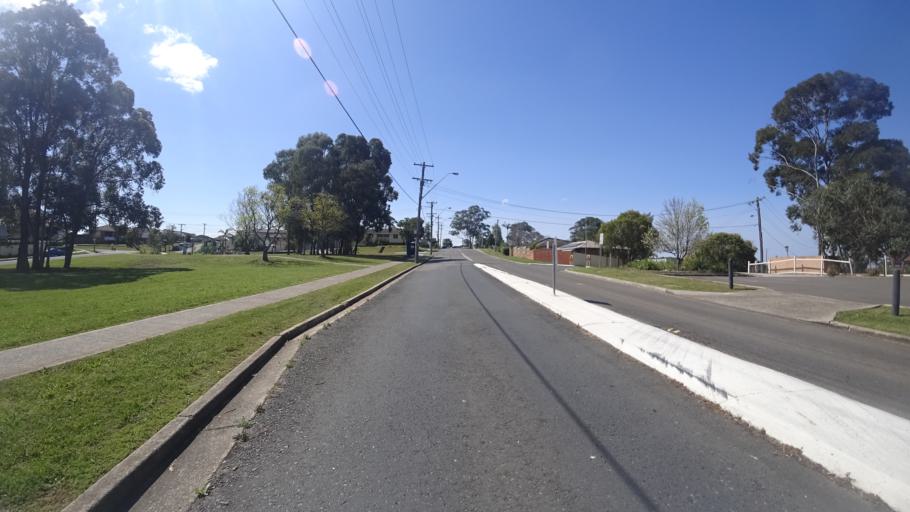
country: AU
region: New South Wales
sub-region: Fairfield
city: Cabramatta West
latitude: -33.9023
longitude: 150.9085
